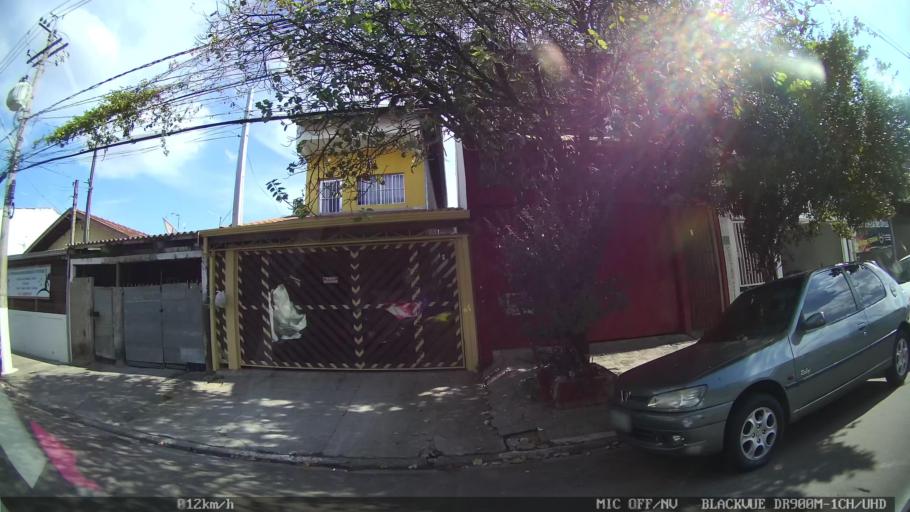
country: BR
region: Sao Paulo
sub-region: Hortolandia
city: Hortolandia
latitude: -22.8980
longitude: -47.2440
